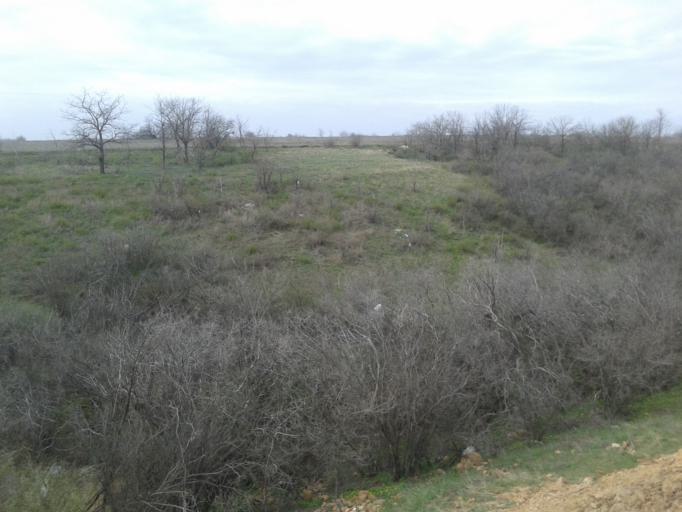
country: RU
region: Volgograd
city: Volgograd
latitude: 48.6631
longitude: 44.4065
